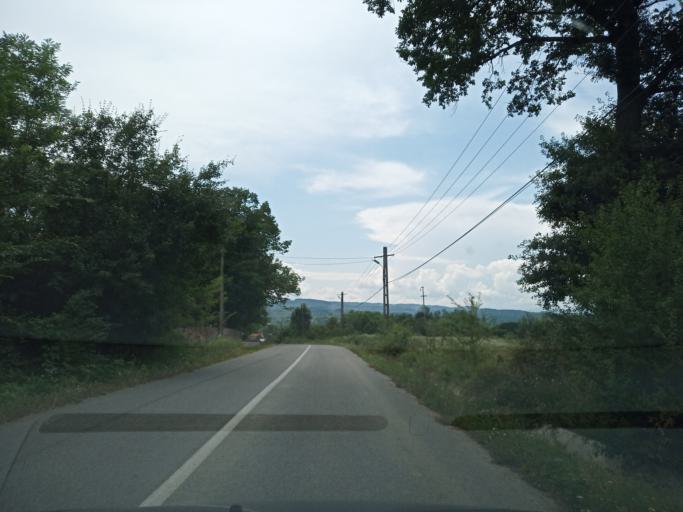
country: RO
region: Gorj
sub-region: Comuna Godinesti
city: Godinesti
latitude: 44.9819
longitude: 22.9591
